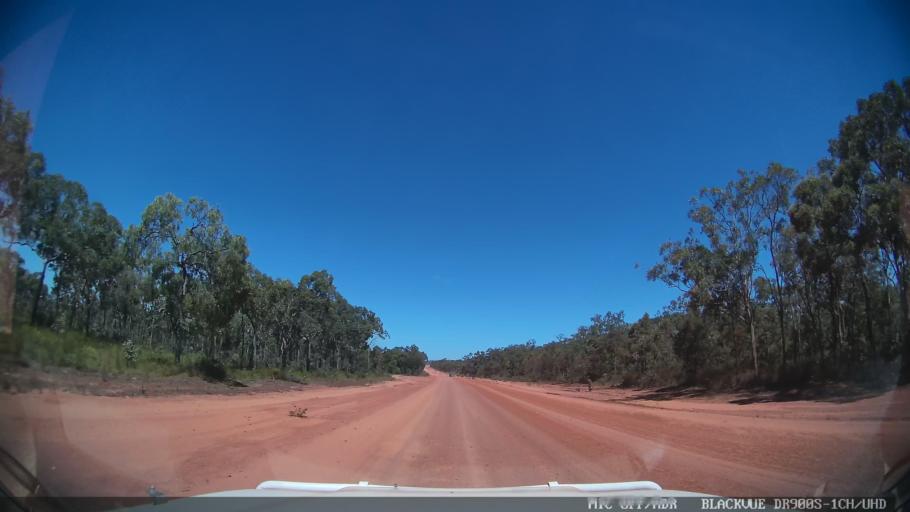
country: AU
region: Queensland
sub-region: Torres
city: Thursday Island
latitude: -11.3647
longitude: 142.3461
